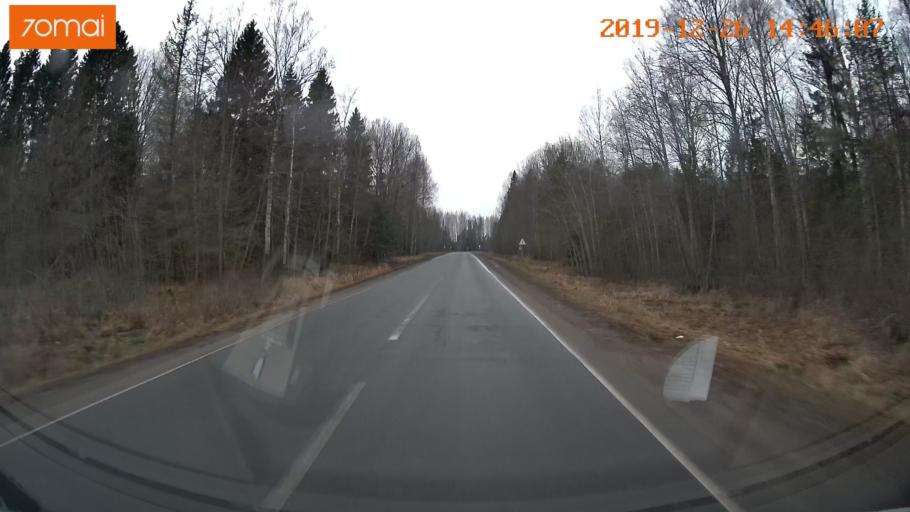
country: RU
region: Jaroslavl
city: Poshekhon'ye
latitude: 58.3347
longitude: 39.0238
